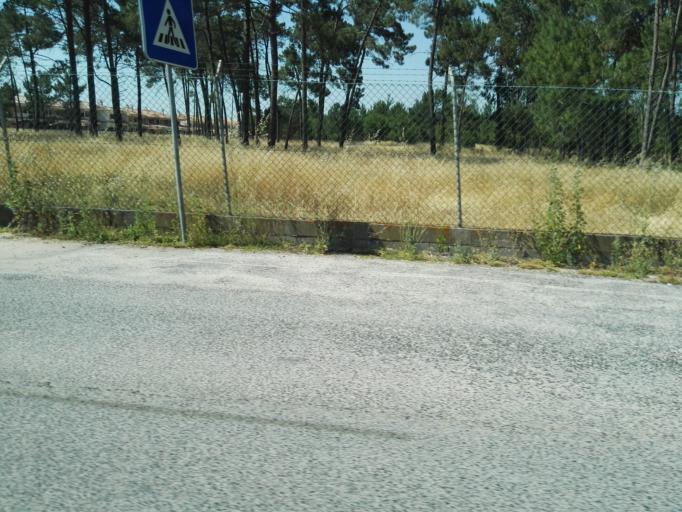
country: PT
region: Santarem
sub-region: Benavente
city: Samora Correia
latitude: 38.9363
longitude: -8.8559
